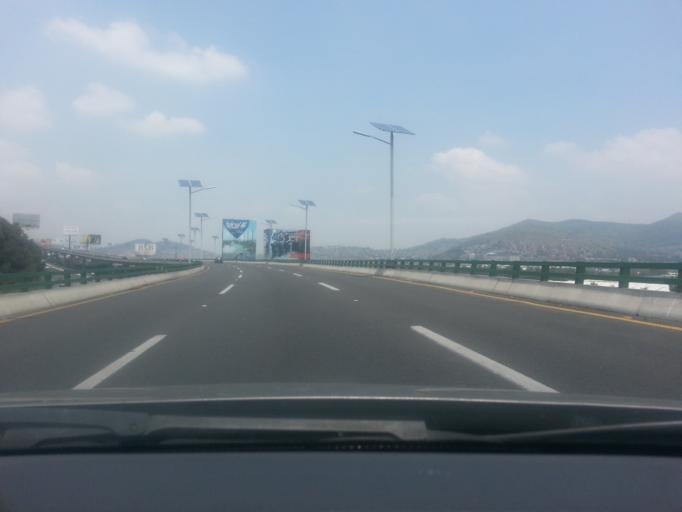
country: MX
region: Mexico
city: Tlalnepantla
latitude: 19.5526
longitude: -99.2065
